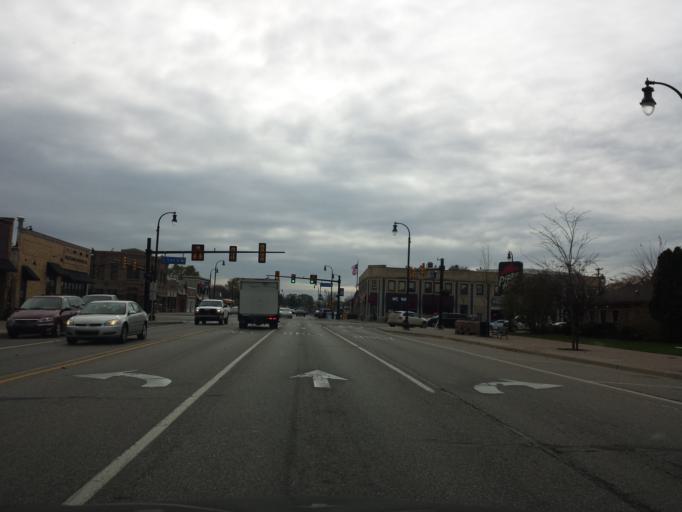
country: US
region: Michigan
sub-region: Oakland County
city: Clawson
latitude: 42.5341
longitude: -83.1464
